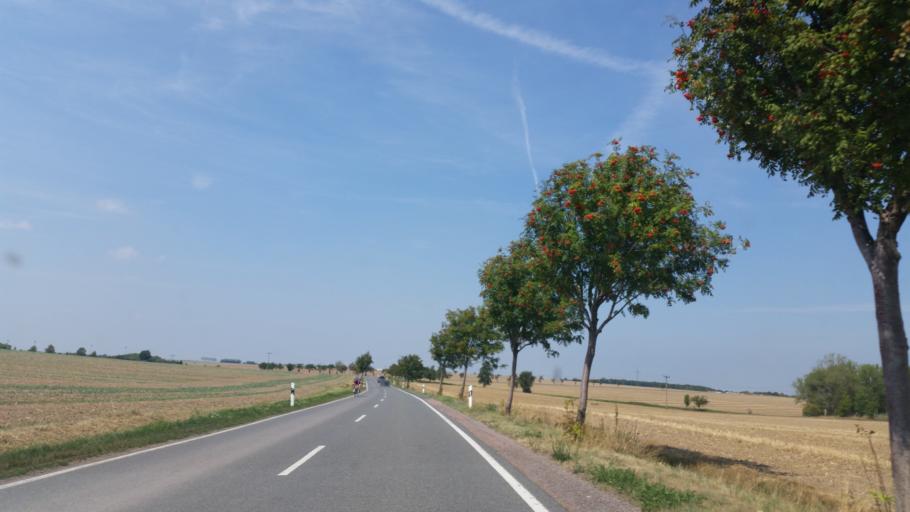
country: DE
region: Saxony
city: Wilsdruff
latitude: 51.0649
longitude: 13.5538
